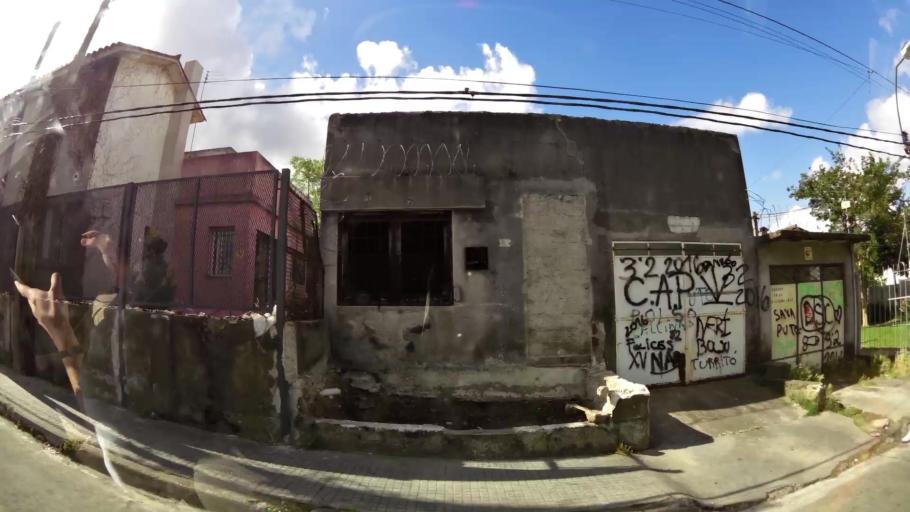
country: UY
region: Canelones
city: La Paz
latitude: -34.8083
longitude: -56.2209
